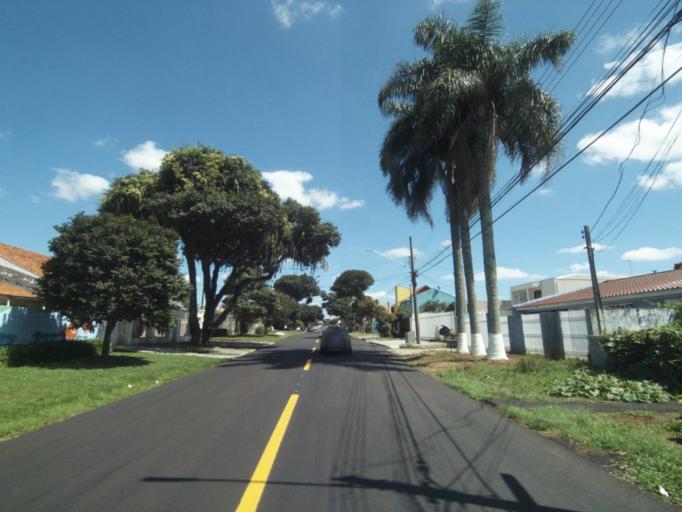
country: BR
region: Parana
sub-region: Pinhais
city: Pinhais
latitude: -25.4400
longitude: -49.2187
